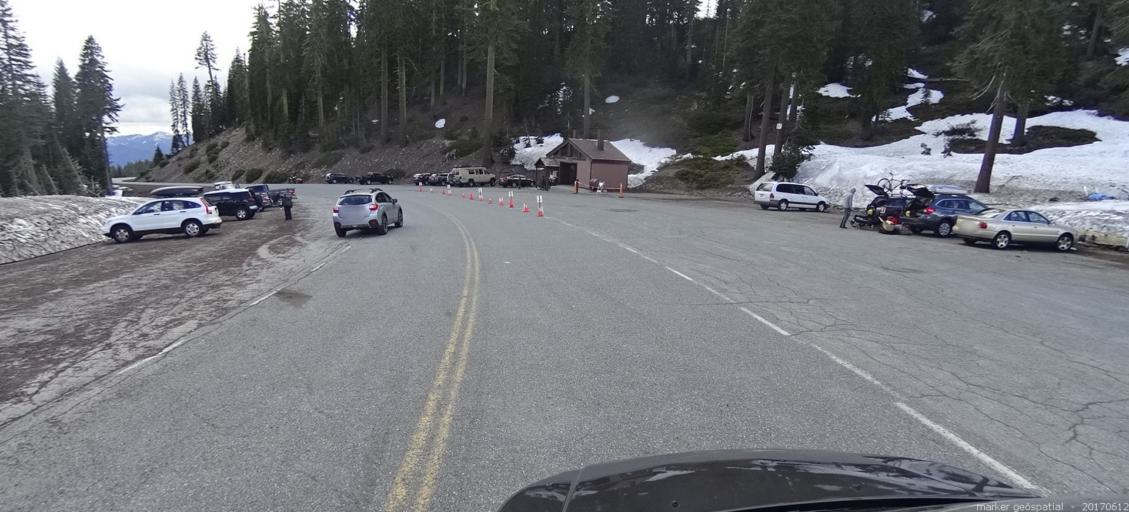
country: US
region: California
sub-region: Siskiyou County
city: Mount Shasta
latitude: 41.3539
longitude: -122.2332
